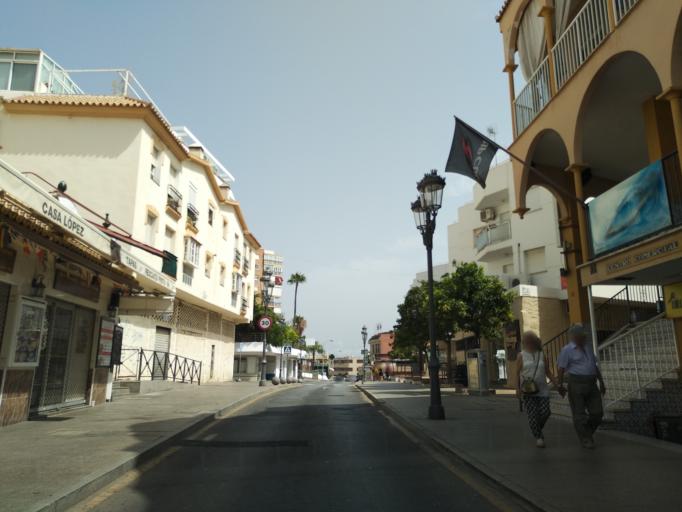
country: ES
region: Andalusia
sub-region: Provincia de Malaga
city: Torremolinos
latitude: 36.6228
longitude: -4.4975
